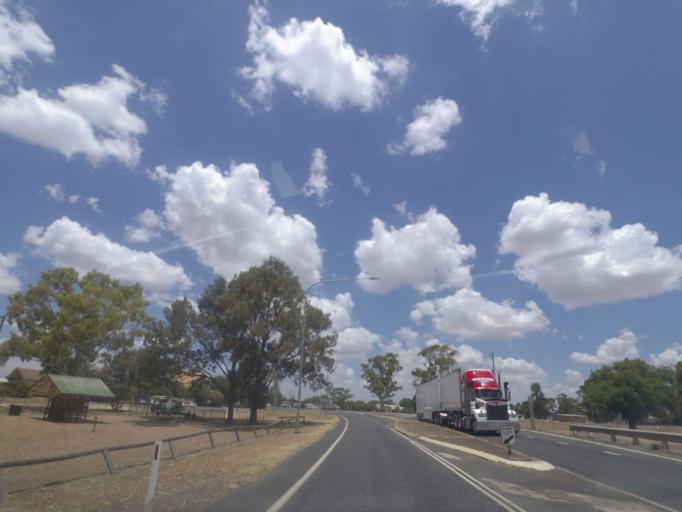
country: AU
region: Queensland
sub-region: Southern Downs
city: Warwick
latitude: -28.0354
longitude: 151.9879
